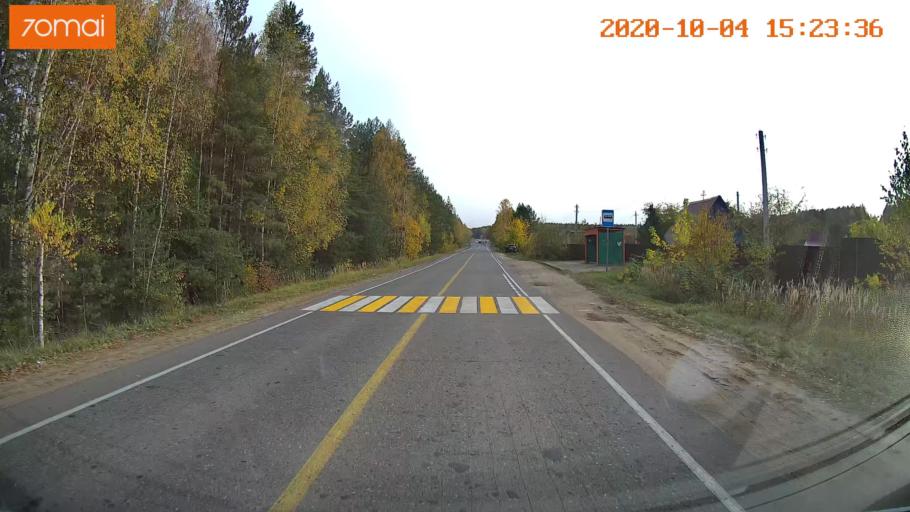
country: RU
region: Ivanovo
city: Bogorodskoye
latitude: 57.0721
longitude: 40.9505
